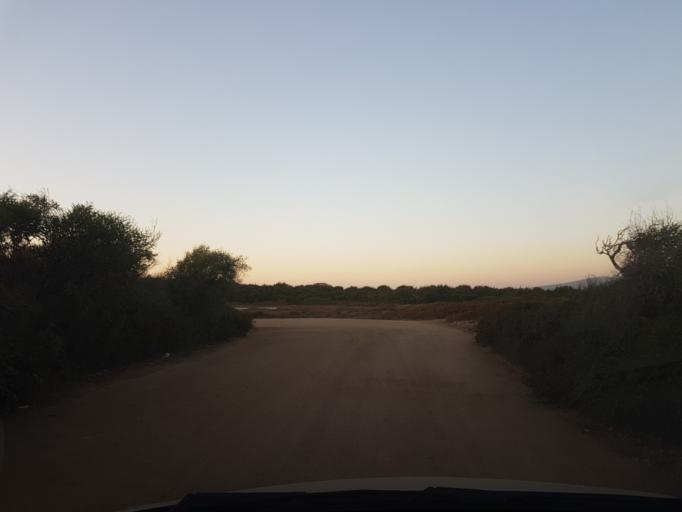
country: IT
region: Sardinia
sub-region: Provincia di Oristano
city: Riola Sardo
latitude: 40.0430
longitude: 8.4015
